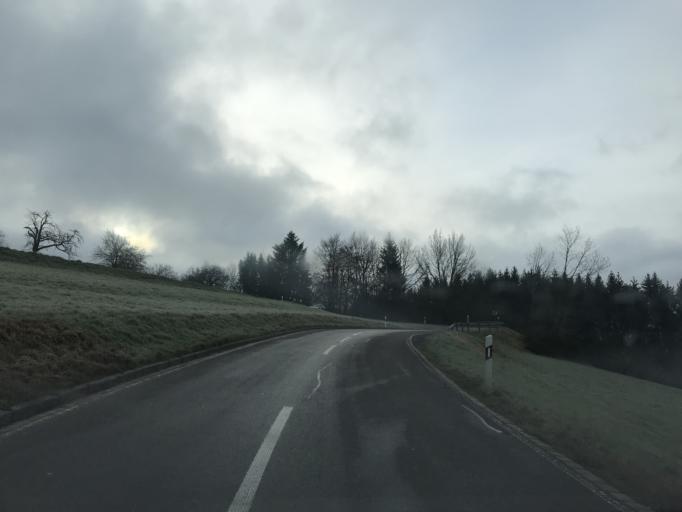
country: DE
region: Baden-Wuerttemberg
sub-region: Freiburg Region
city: Wehr
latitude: 47.6209
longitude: 7.9104
